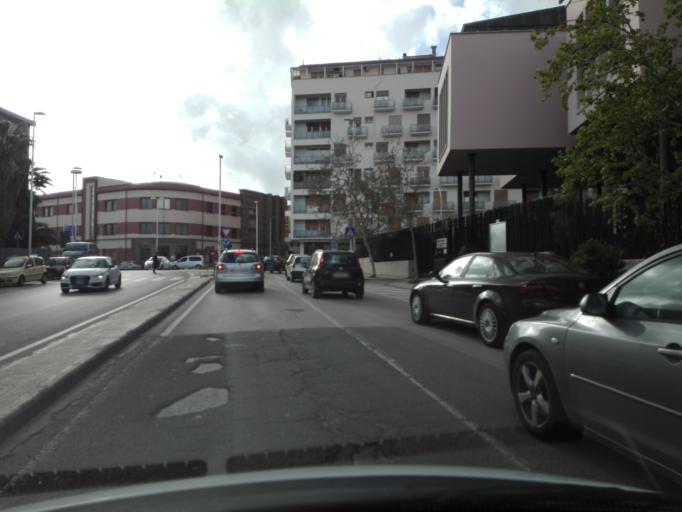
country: IT
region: Sardinia
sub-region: Provincia di Sassari
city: Sassari
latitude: 40.7188
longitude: 8.5716
